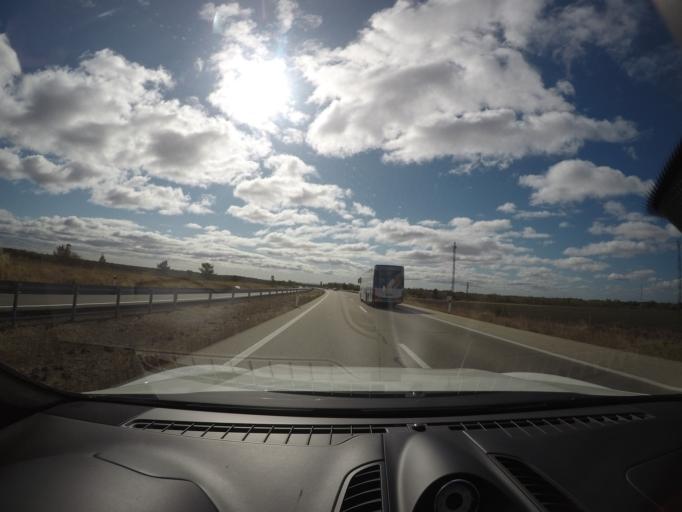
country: ES
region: Castille and Leon
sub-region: Provincia de Leon
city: Cimanes del Tejar
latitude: 42.6187
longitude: -5.7386
